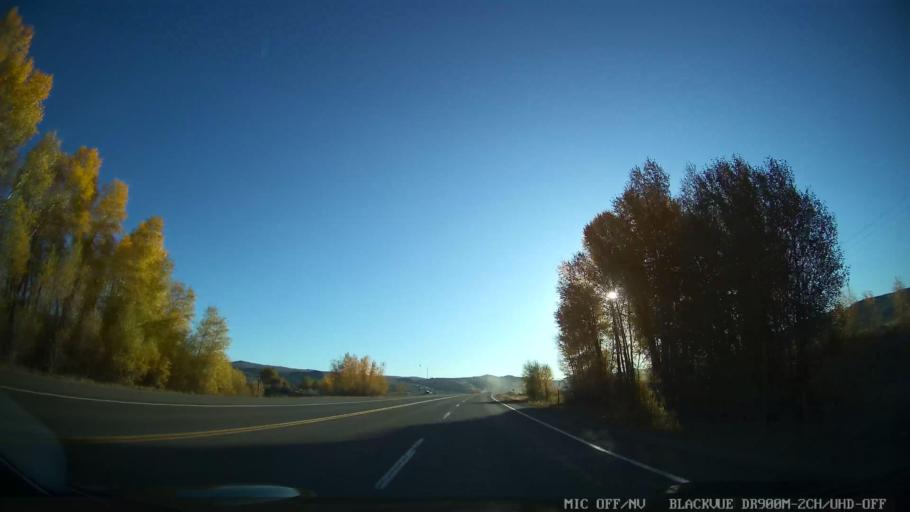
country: US
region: Colorado
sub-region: Grand County
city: Hot Sulphur Springs
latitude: 40.0675
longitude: -106.2252
